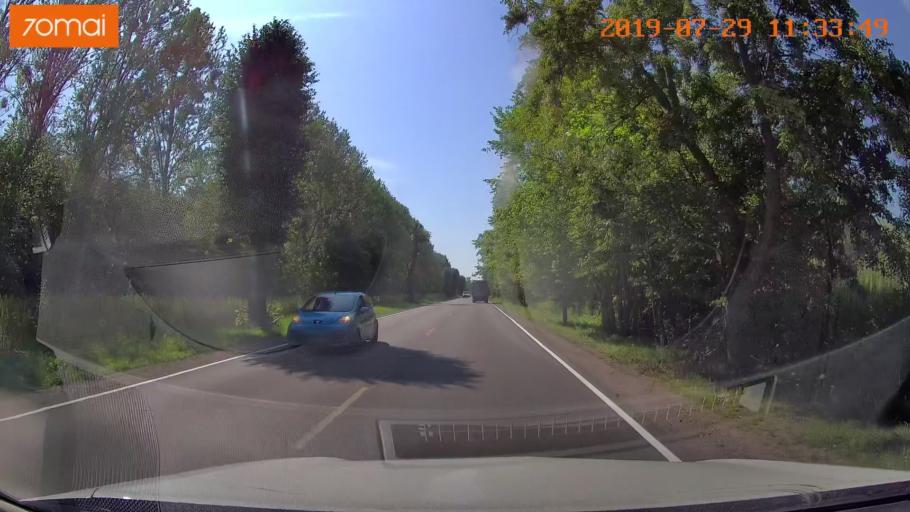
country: RU
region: Kaliningrad
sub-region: Gorod Kaliningrad
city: Kaliningrad
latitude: 54.6613
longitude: 20.5409
